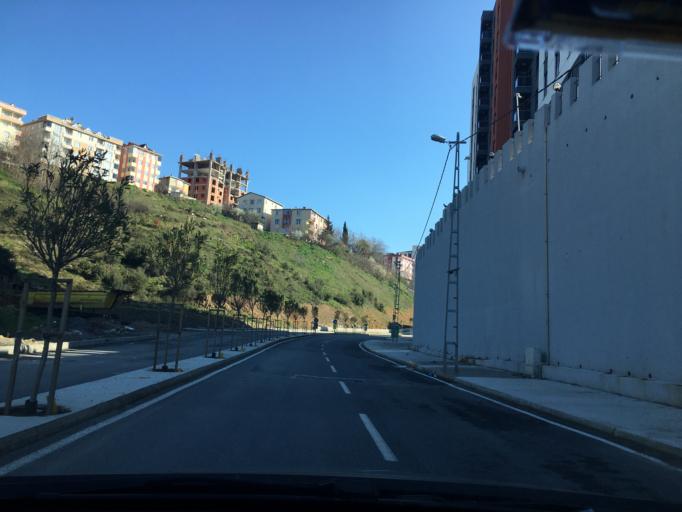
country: TR
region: Istanbul
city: Icmeler
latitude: 40.8717
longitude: 29.3015
